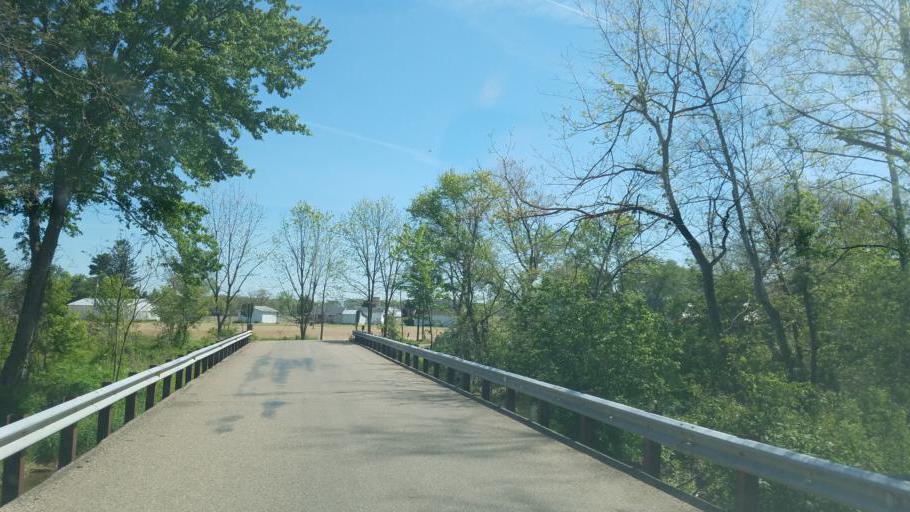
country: US
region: Ohio
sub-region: Knox County
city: Fredericktown
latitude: 40.4391
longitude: -82.5113
